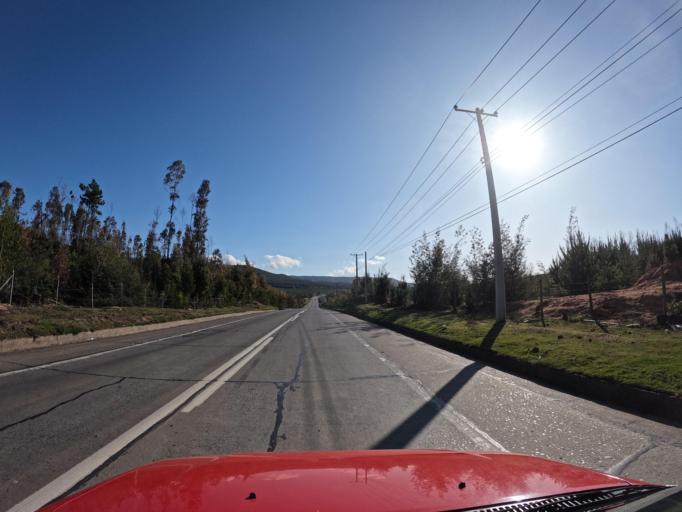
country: CL
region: Maule
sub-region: Provincia de Talca
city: Constitucion
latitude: -35.4449
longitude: -72.3051
